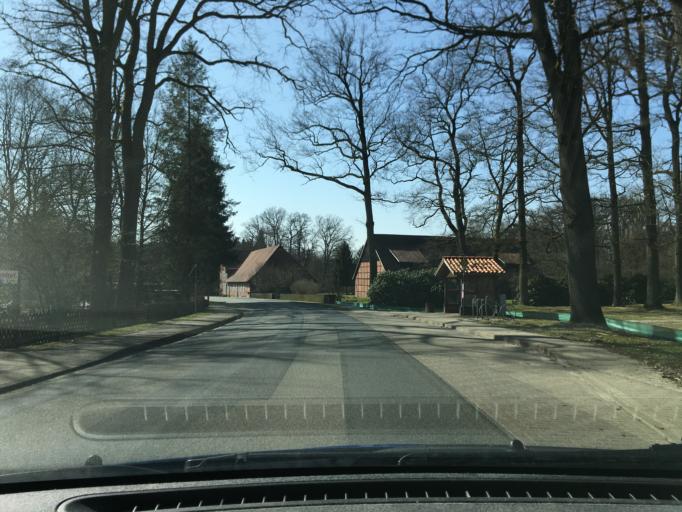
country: DE
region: Lower Saxony
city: Unterluss
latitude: 52.8285
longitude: 10.2138
